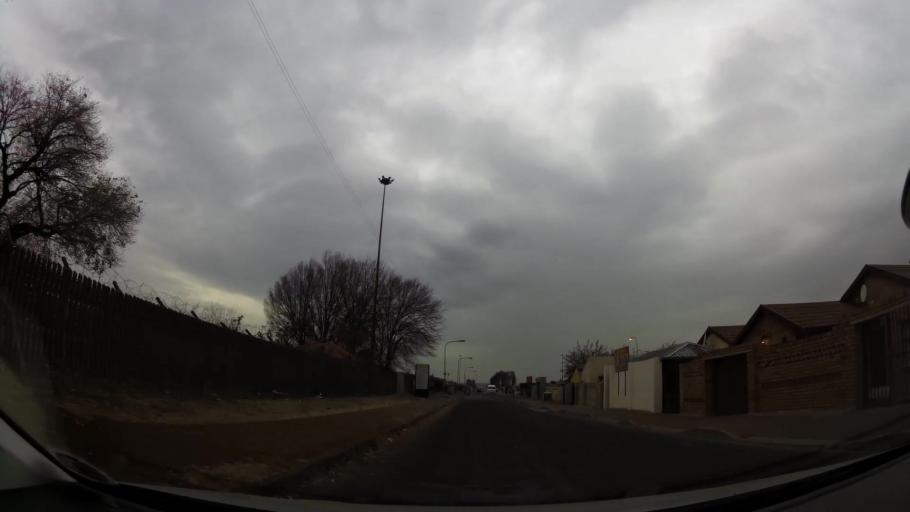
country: ZA
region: Gauteng
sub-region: City of Johannesburg Metropolitan Municipality
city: Soweto
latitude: -26.2531
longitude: 27.8713
